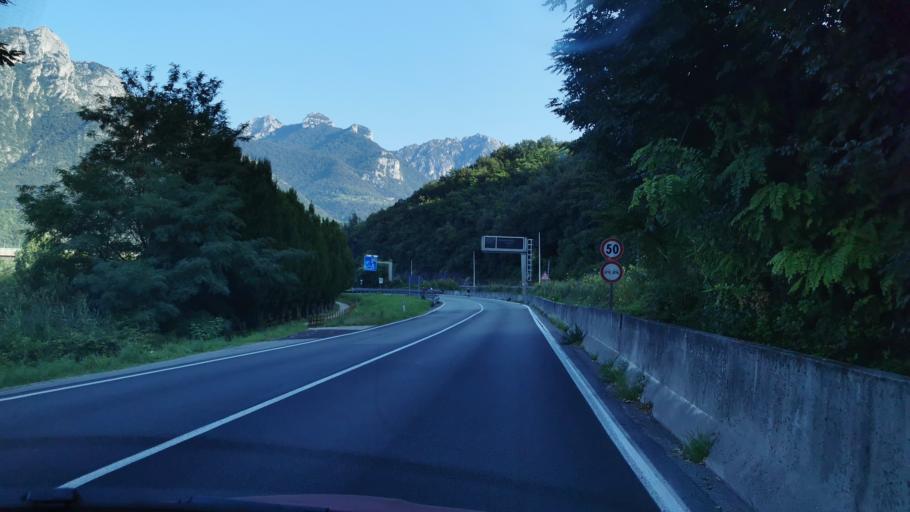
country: IT
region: Lombardy
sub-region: Provincia di Lecco
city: Sala al Barro
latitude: 45.8252
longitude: 9.3564
